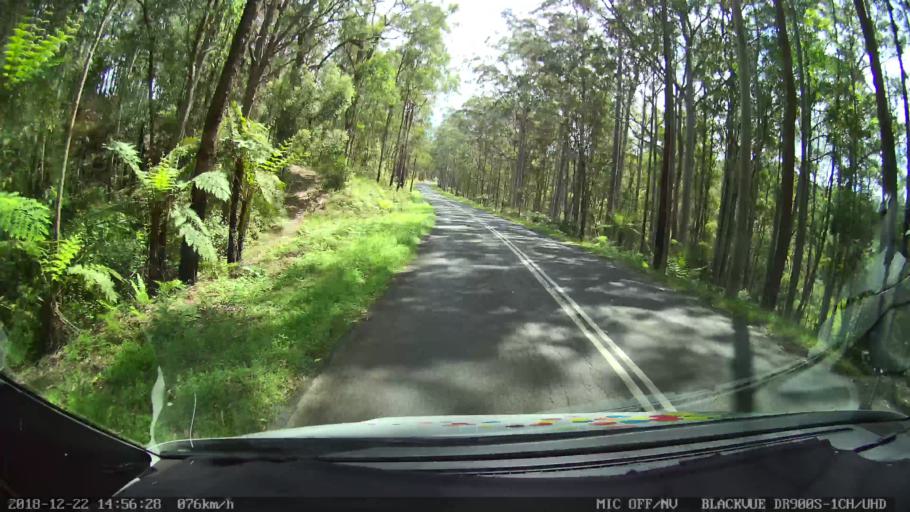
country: AU
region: New South Wales
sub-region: Bellingen
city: Dorrigo
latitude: -30.2328
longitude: 152.5121
